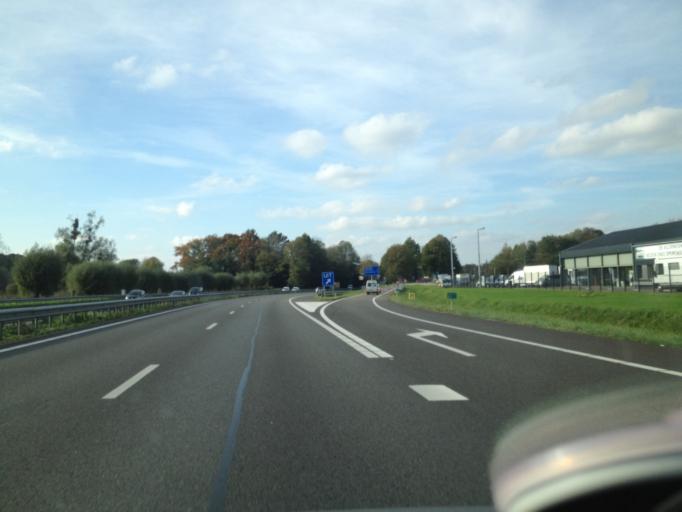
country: NL
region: Limburg
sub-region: Gemeente Schinnen
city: Puth
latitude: 50.9423
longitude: 5.8526
